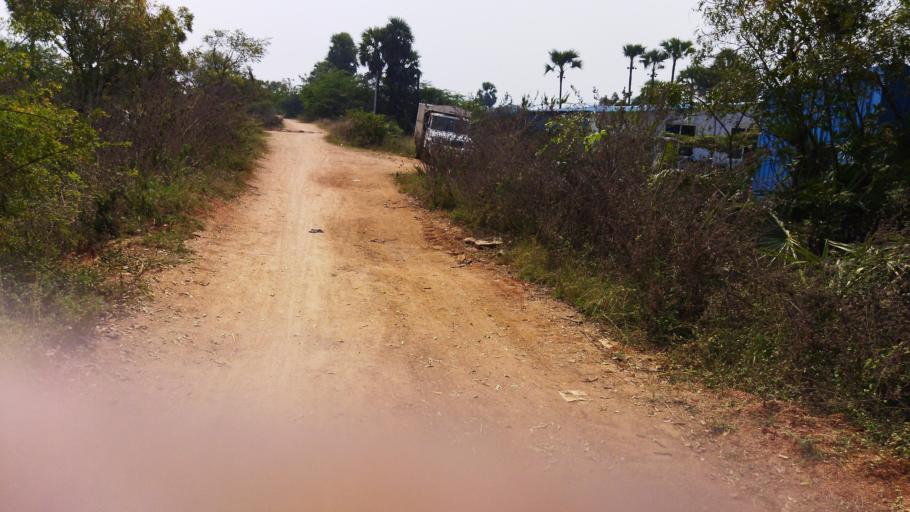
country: IN
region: Telangana
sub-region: Nalgonda
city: Nalgonda
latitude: 17.1519
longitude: 79.4094
